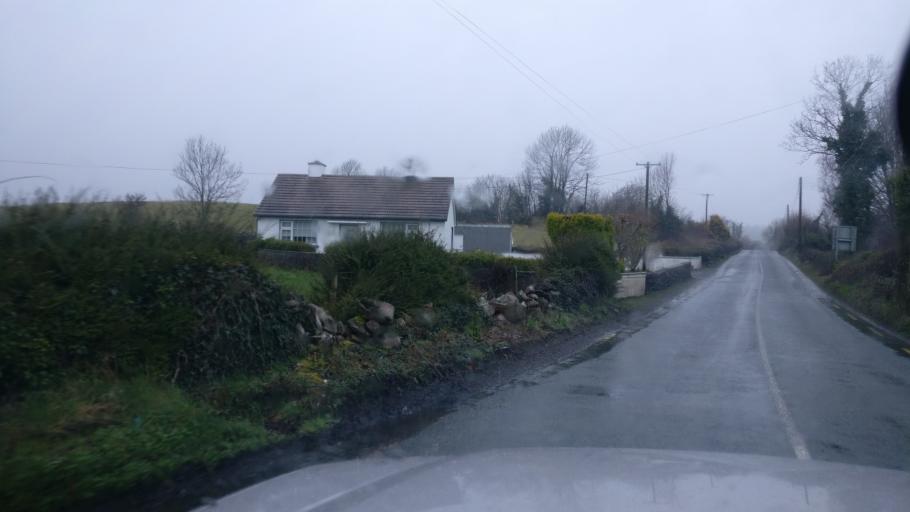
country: IE
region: Connaught
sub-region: County Galway
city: Loughrea
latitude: 53.1326
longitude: -8.4599
